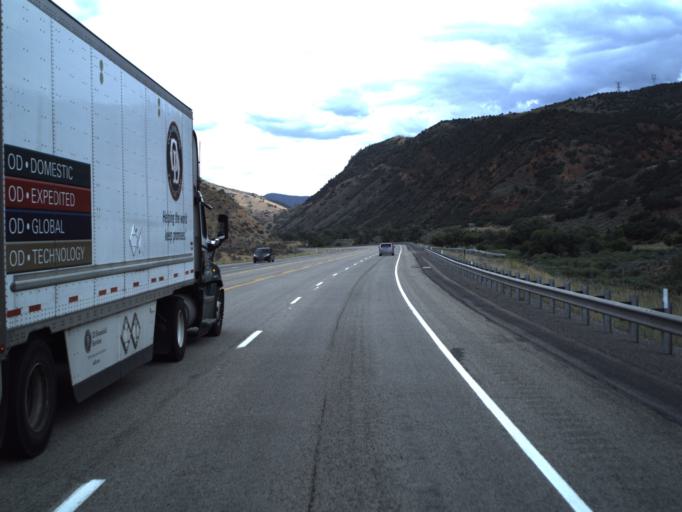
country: US
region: Utah
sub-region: Utah County
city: Mapleton
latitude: 39.9963
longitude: -111.4440
